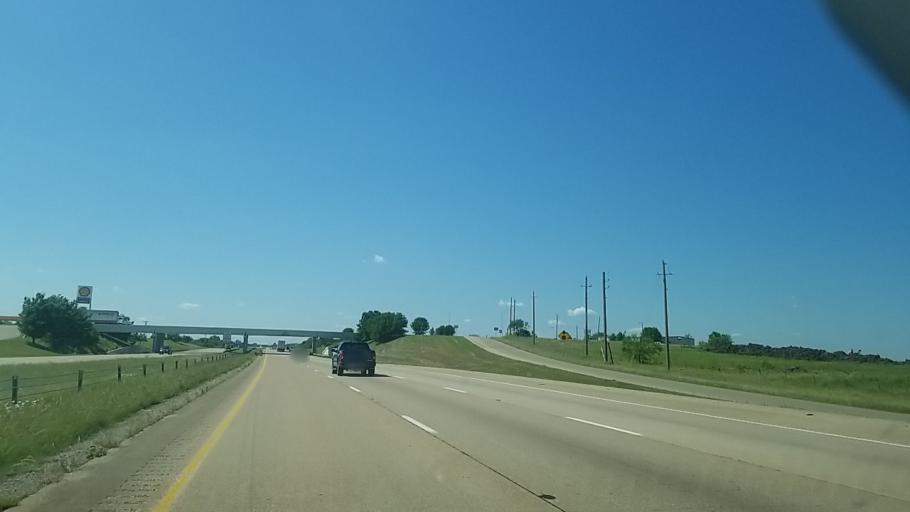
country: US
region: Texas
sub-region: Ellis County
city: Ennis
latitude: 32.3579
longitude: -96.6305
